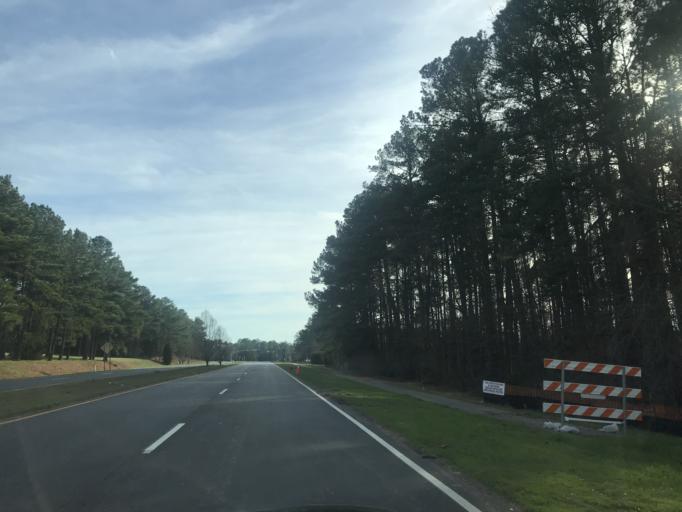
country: US
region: North Carolina
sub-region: Wake County
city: Morrisville
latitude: 35.8988
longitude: -78.8590
